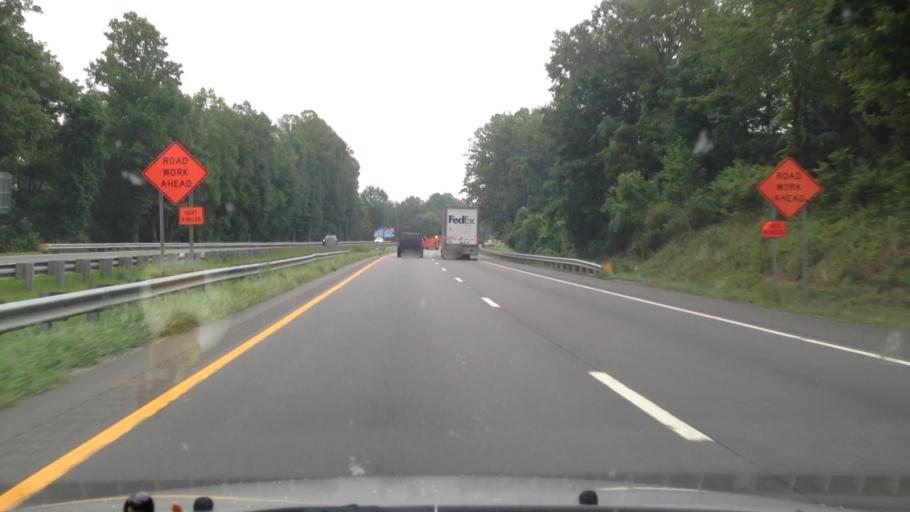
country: US
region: North Carolina
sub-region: Forsyth County
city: Kernersville
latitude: 36.1036
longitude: -80.0317
